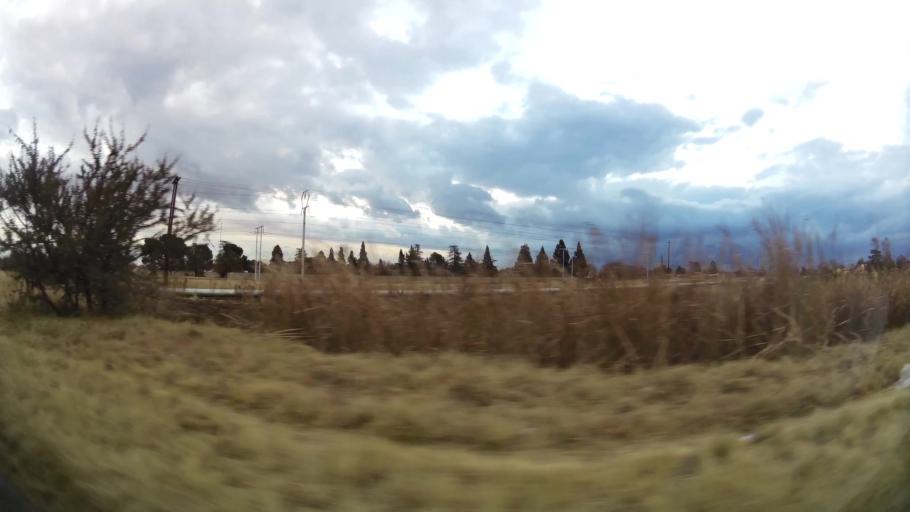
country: ZA
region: Orange Free State
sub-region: Lejweleputswa District Municipality
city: Welkom
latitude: -27.9694
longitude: 26.7754
